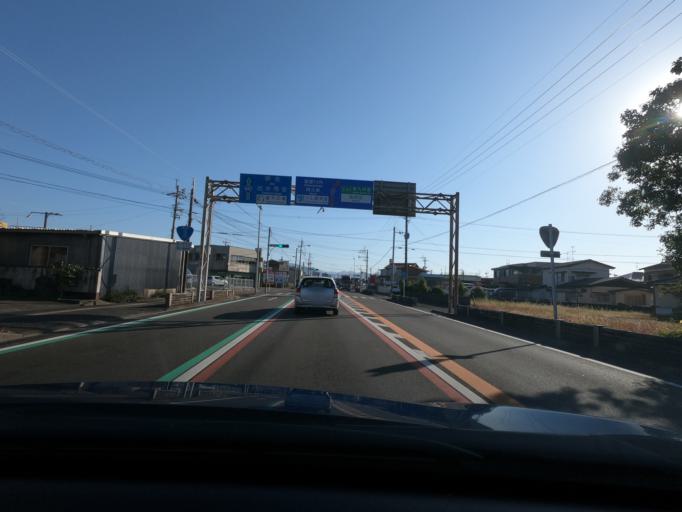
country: JP
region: Kagoshima
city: Izumi
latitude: 32.1185
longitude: 130.3400
